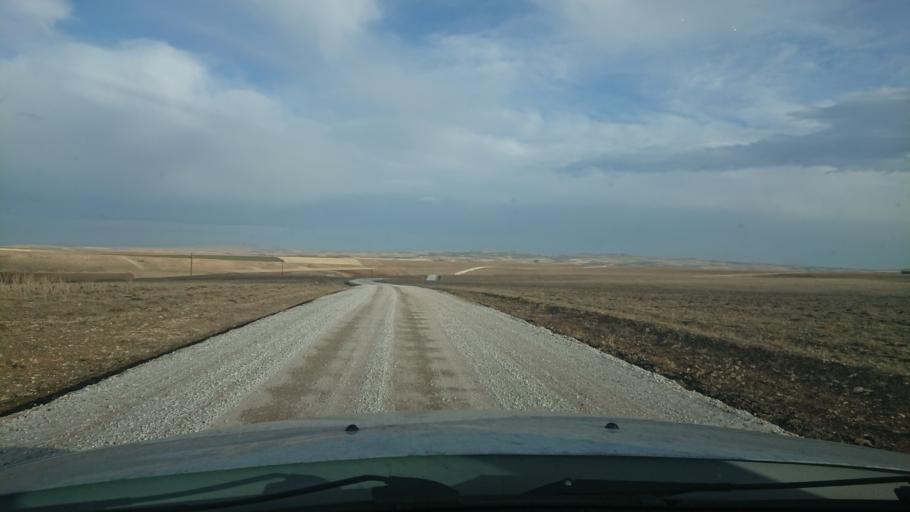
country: TR
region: Aksaray
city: Agacoren
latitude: 38.7313
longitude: 33.8697
